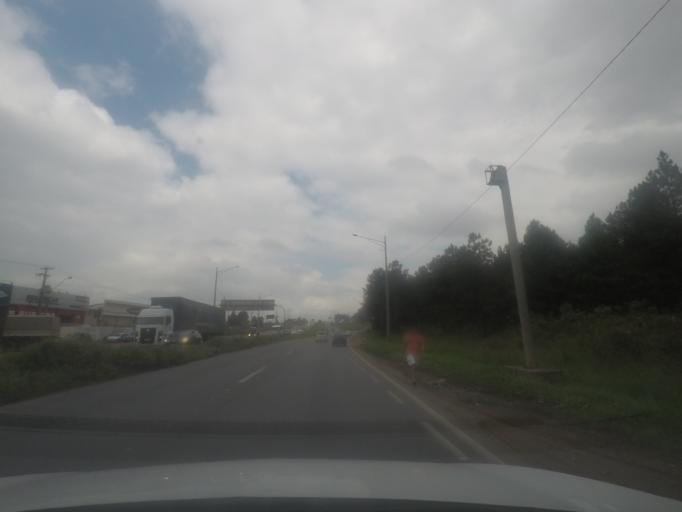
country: BR
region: Parana
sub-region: Sao Jose Dos Pinhais
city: Sao Jose dos Pinhais
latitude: -25.5383
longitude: -49.3018
